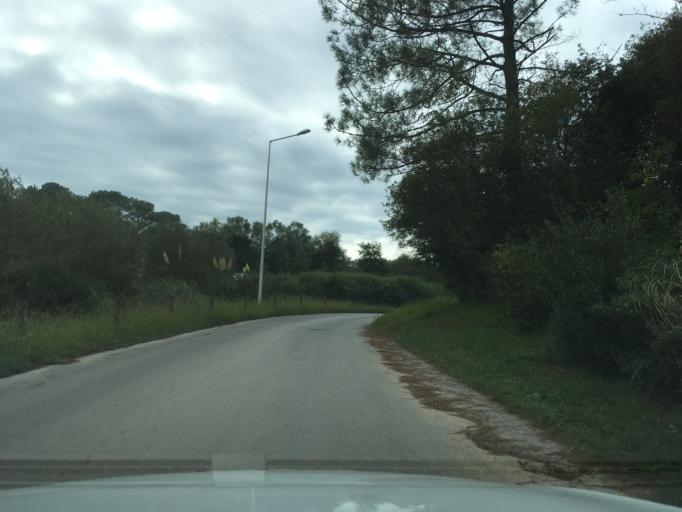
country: FR
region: Aquitaine
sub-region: Departement des Pyrenees-Atlantiques
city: Biarritz
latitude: 43.4594
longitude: -1.5670
